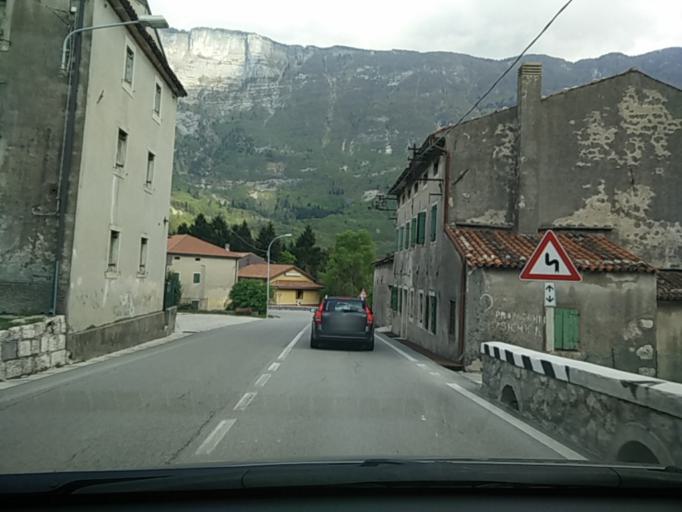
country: IT
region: Veneto
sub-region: Provincia di Belluno
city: Farra d'Alpago
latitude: 46.0781
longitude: 12.3341
